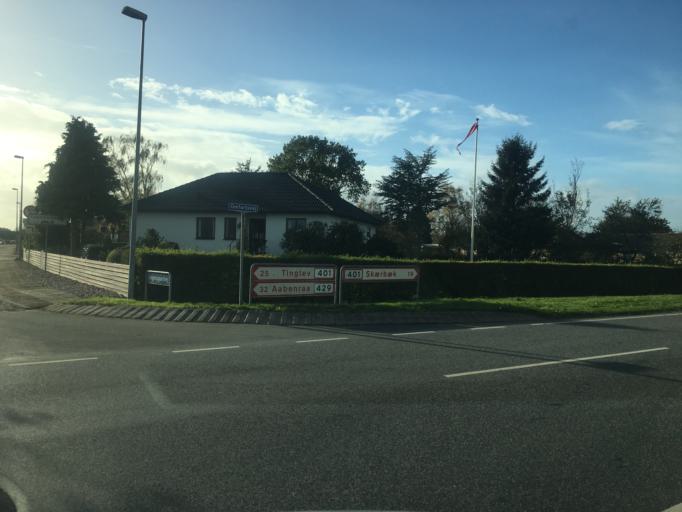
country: DK
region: South Denmark
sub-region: Tonder Kommune
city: Logumkloster
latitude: 55.0601
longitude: 8.9640
